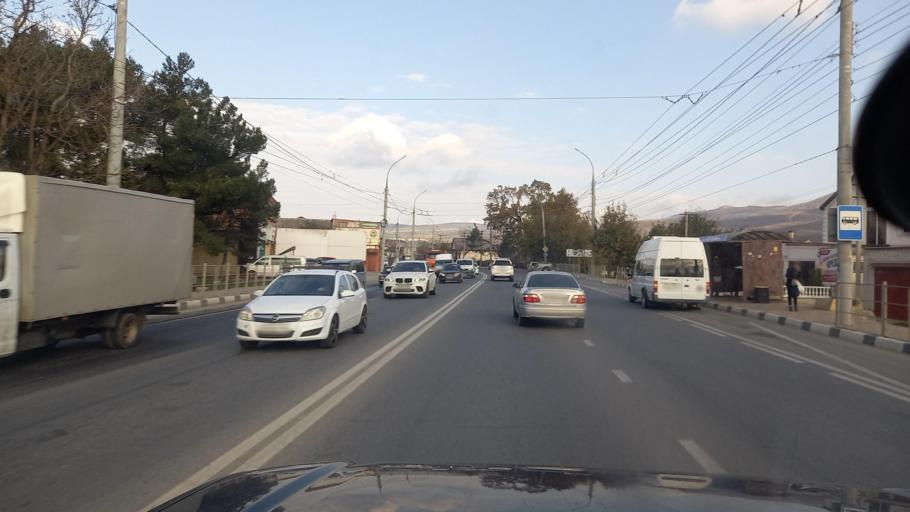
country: RU
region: Krasnodarskiy
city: Gayduk
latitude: 44.7553
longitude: 37.7260
